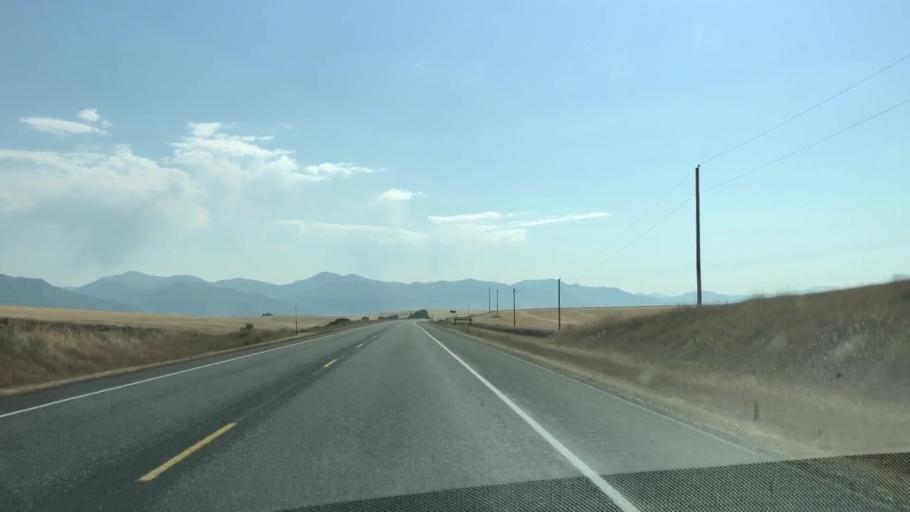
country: US
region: Idaho
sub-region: Madison County
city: Rexburg
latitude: 43.5861
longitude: -111.5902
